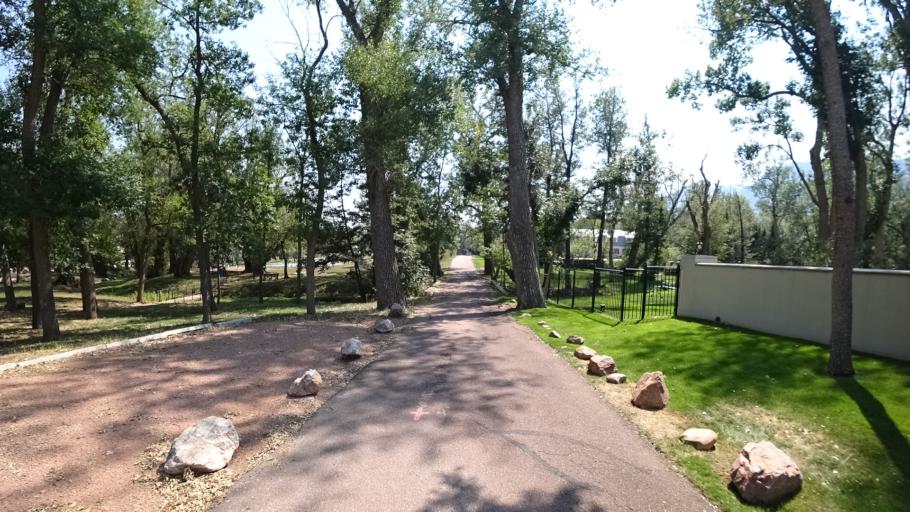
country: US
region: Colorado
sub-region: El Paso County
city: Colorado Springs
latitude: 38.7900
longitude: -104.8426
